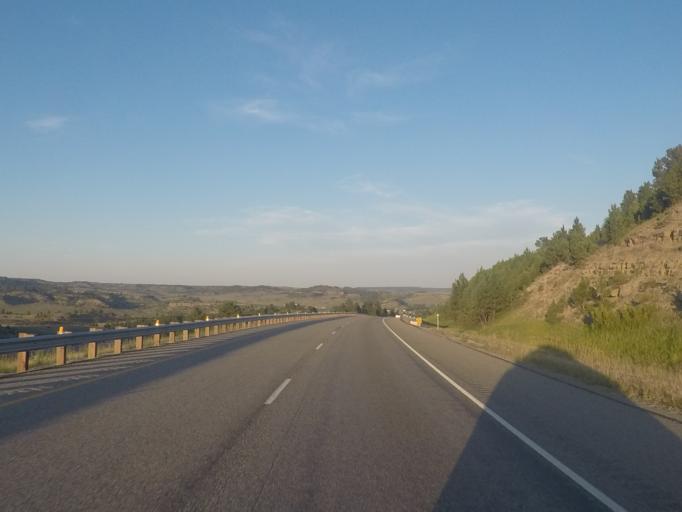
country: US
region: Montana
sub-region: Stillwater County
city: Columbus
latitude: 45.6579
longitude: -109.2947
